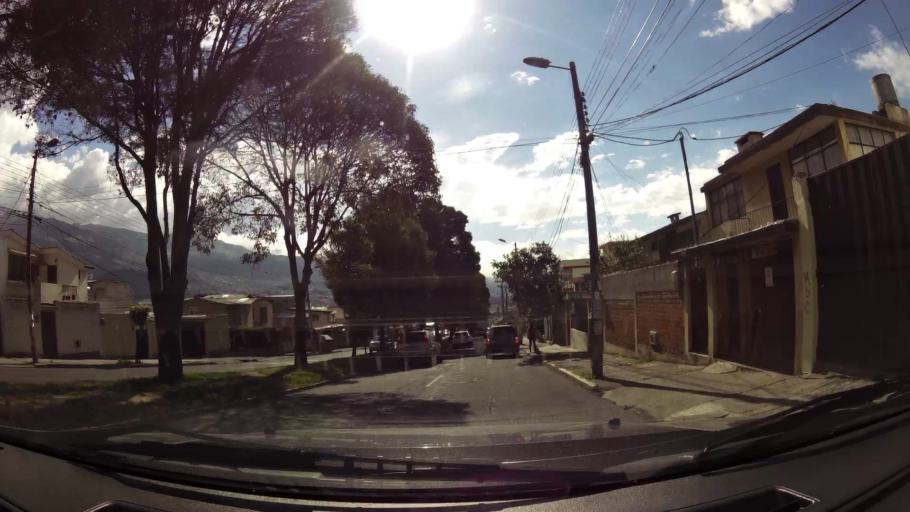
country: EC
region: Pichincha
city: Quito
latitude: -0.1251
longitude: -78.4842
